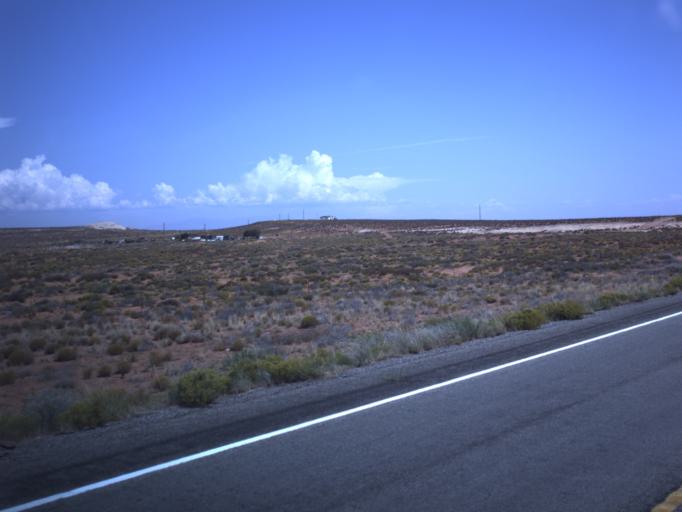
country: US
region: Utah
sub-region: San Juan County
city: Blanding
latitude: 37.0367
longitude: -109.5867
